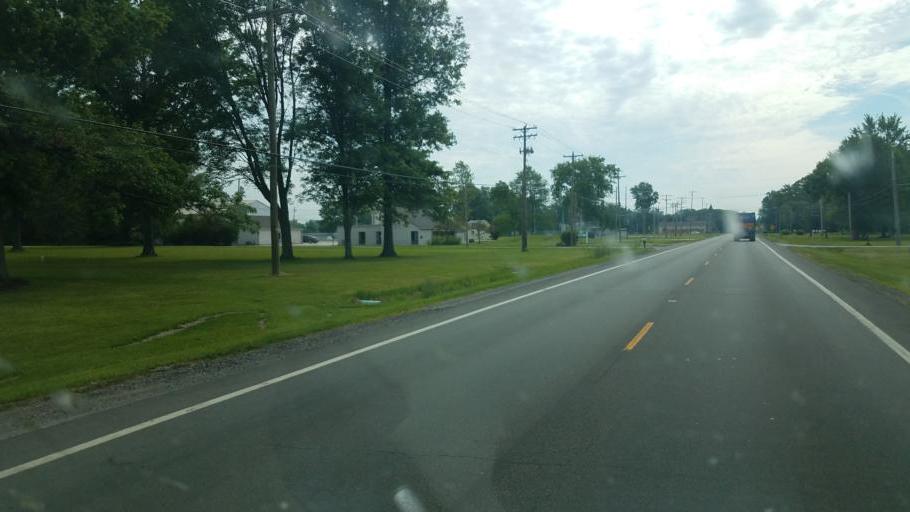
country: US
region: Ohio
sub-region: Cuyahoga County
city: Olmsted Falls
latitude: 41.3128
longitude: -81.9322
